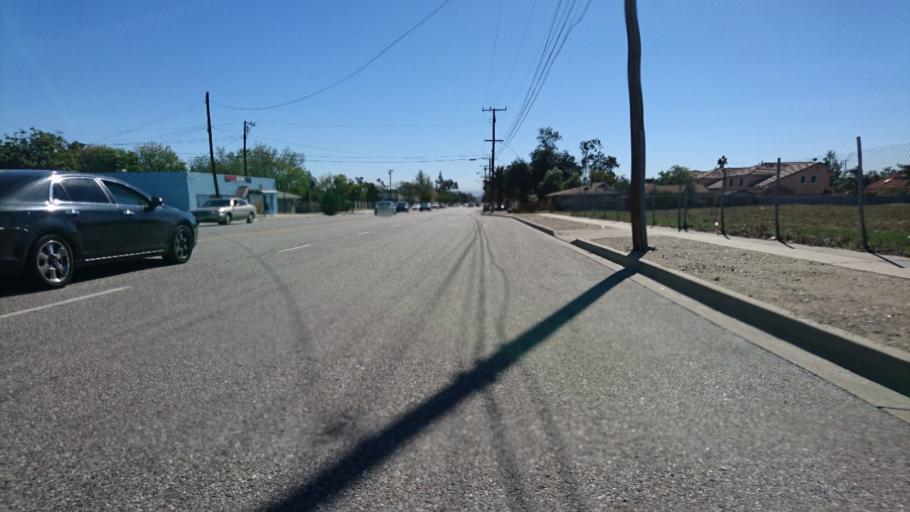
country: US
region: California
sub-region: San Bernardino County
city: Fontana
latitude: 34.1109
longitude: -117.4359
